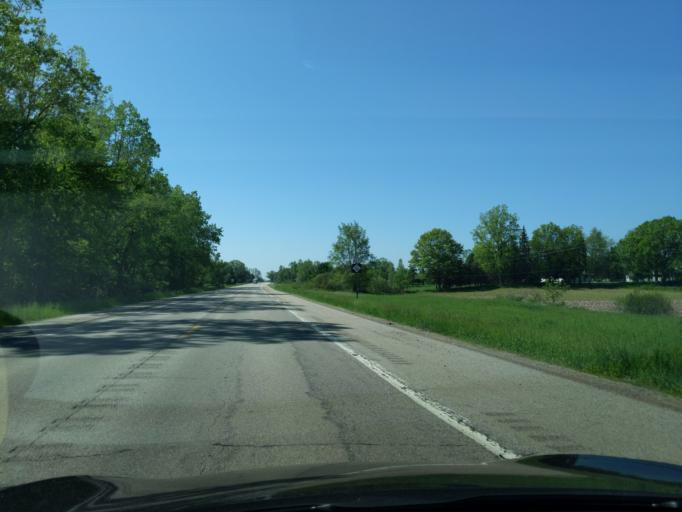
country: US
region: Michigan
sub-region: Ingham County
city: Stockbridge
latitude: 42.5155
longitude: -84.1901
